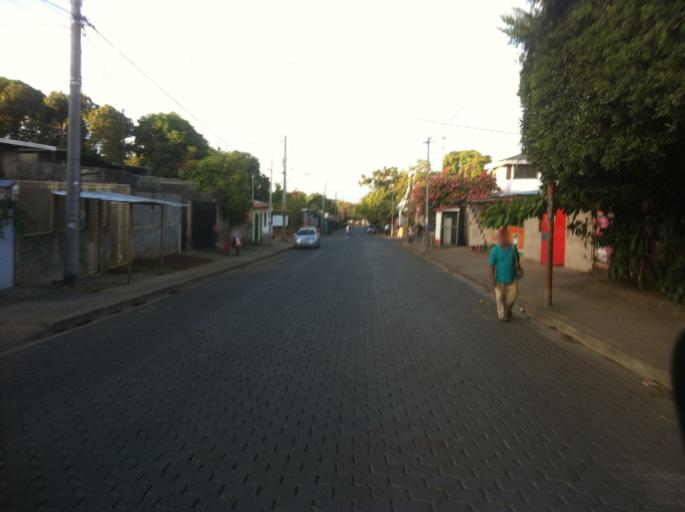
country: NI
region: Managua
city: Managua
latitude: 12.0982
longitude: -86.3028
